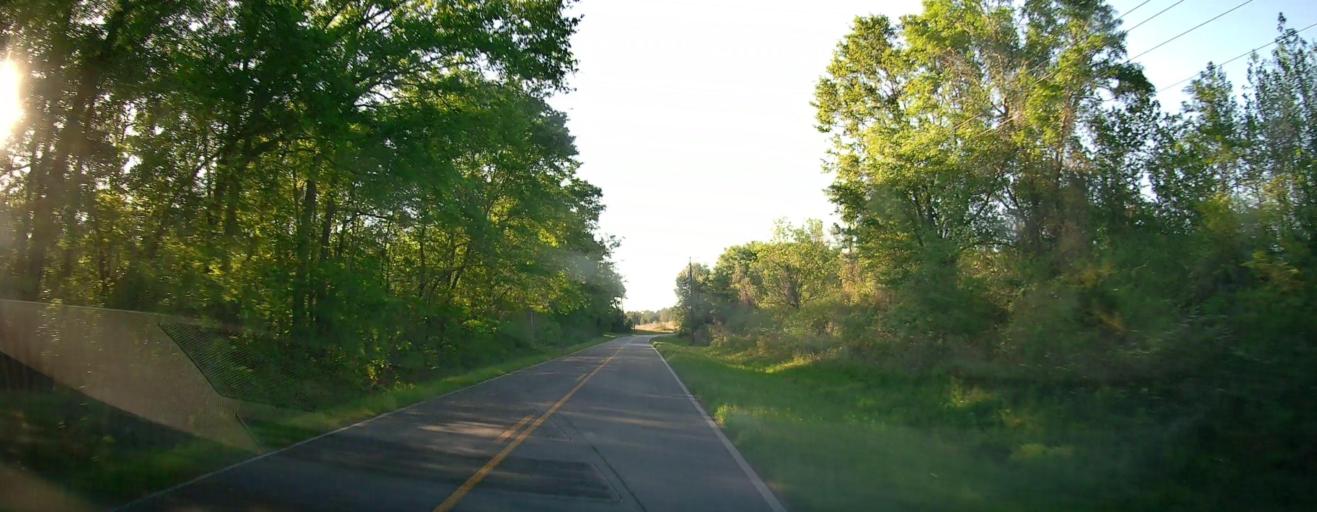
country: US
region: Georgia
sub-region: Macon County
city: Oglethorpe
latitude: 32.2774
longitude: -84.0896
